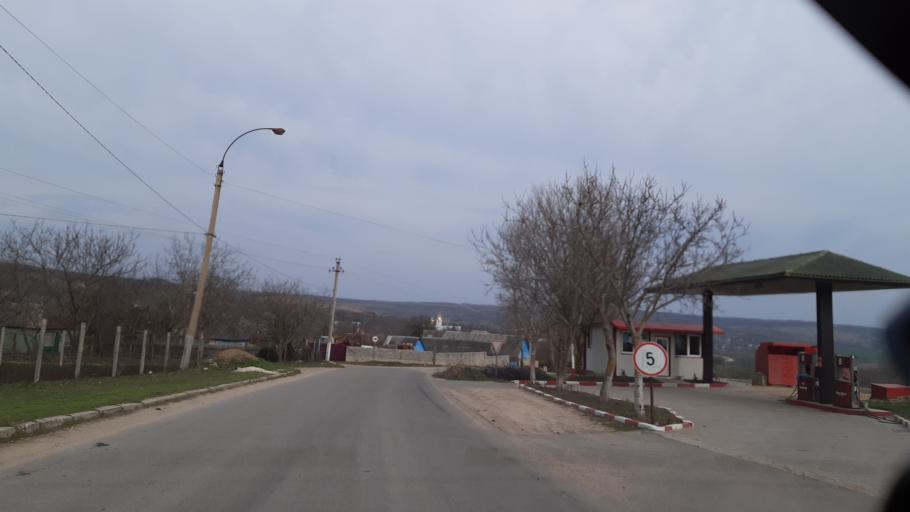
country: MD
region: Soldanesti
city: Soldanesti
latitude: 47.6840
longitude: 28.7736
